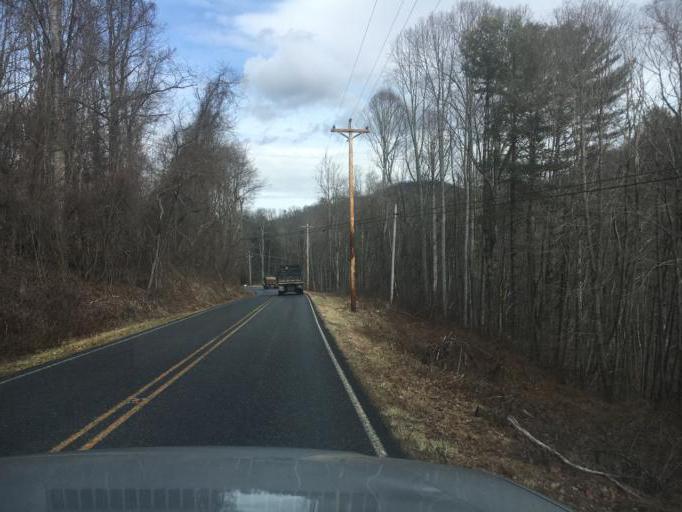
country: US
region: North Carolina
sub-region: Haywood County
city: Canton
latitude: 35.3888
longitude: -82.8143
